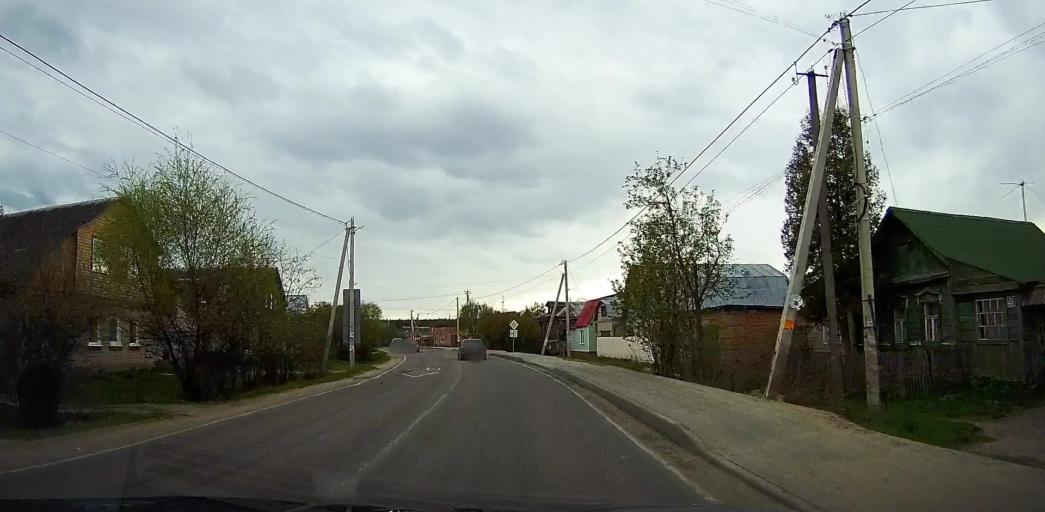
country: RU
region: Moskovskaya
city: Pavlovskiy Posad
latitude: 55.7531
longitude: 38.7015
